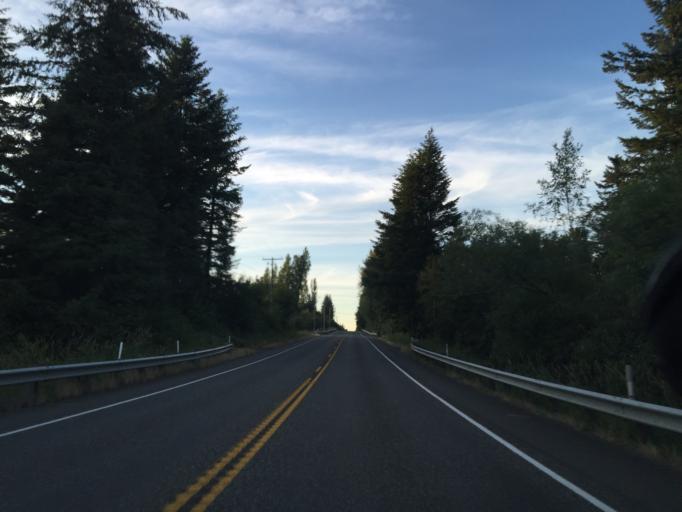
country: US
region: Washington
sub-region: Whatcom County
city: Geneva
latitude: 48.8237
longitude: -122.3769
